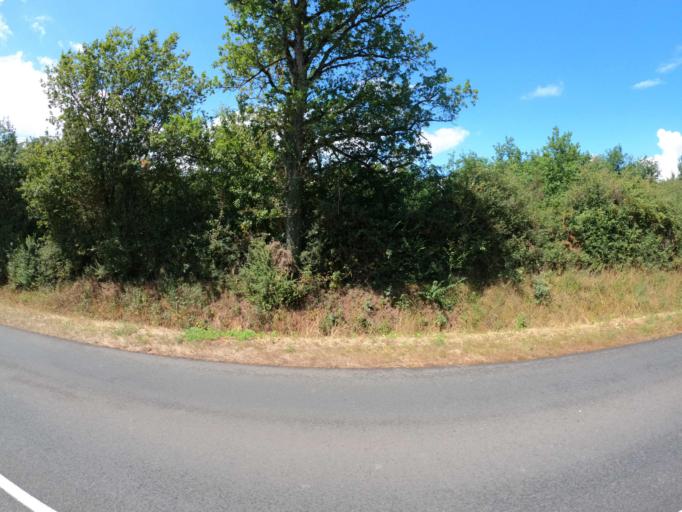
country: FR
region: Pays de la Loire
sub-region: Departement de Maine-et-Loire
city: Champigne
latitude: 47.6183
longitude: -0.5838
